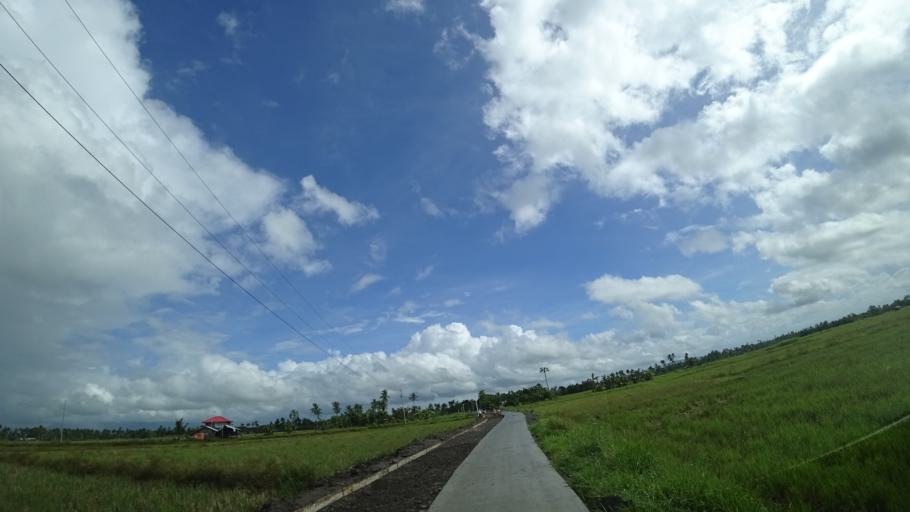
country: PH
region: Eastern Visayas
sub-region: Province of Leyte
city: Cabacungan
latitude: 10.9097
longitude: 124.9777
